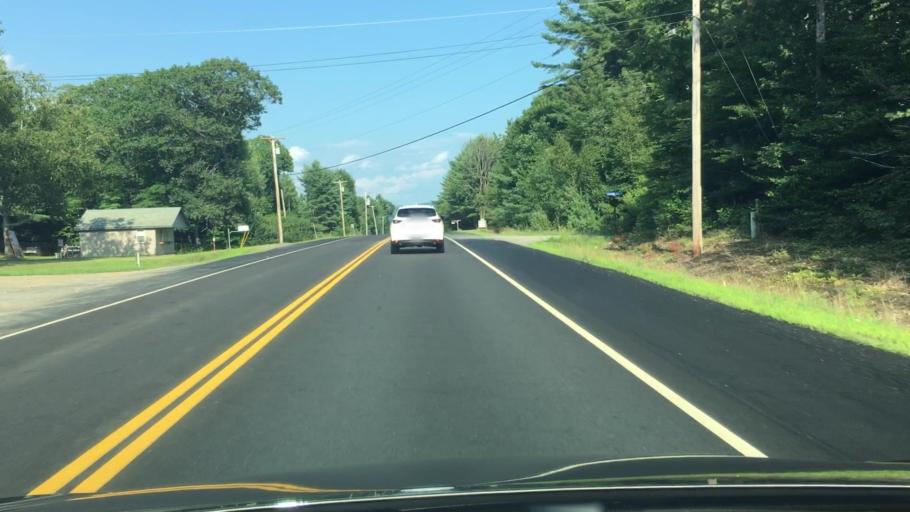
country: US
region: Maine
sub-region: Waldo County
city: Palermo
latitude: 44.4096
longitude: -69.5087
